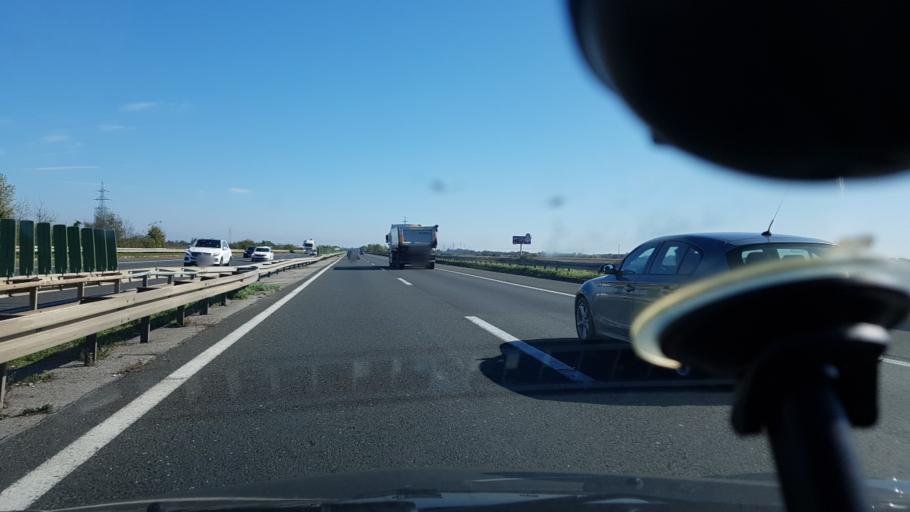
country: HR
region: Grad Zagreb
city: Zadvorsko
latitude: 45.7488
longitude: 15.9361
